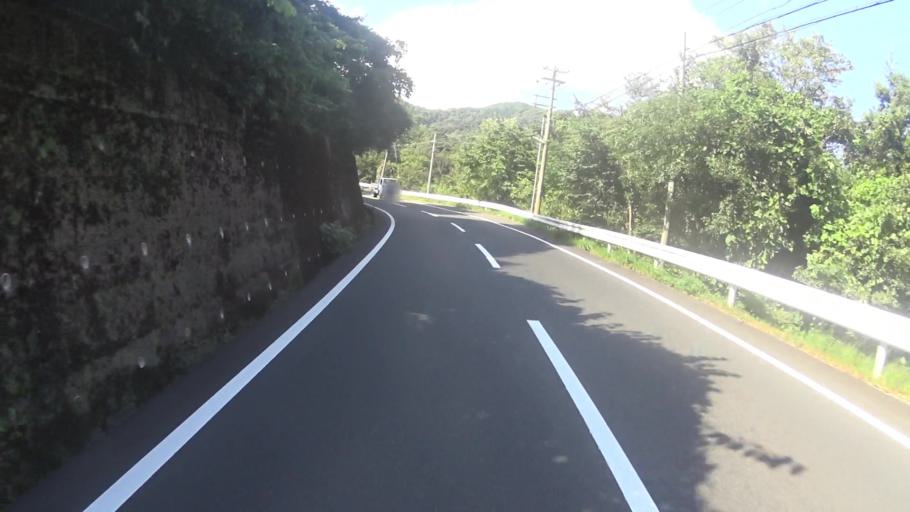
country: JP
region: Kyoto
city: Miyazu
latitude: 35.7060
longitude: 135.2812
